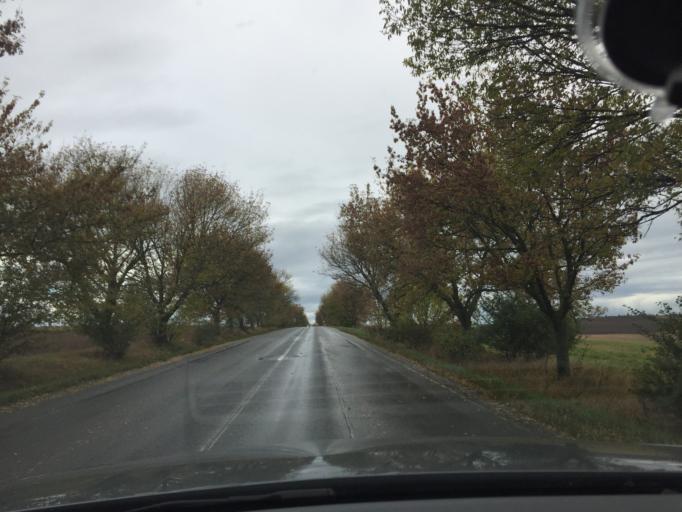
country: CZ
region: Central Bohemia
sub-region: Okres Melnik
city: Veltrusy
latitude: 50.3174
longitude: 14.3021
